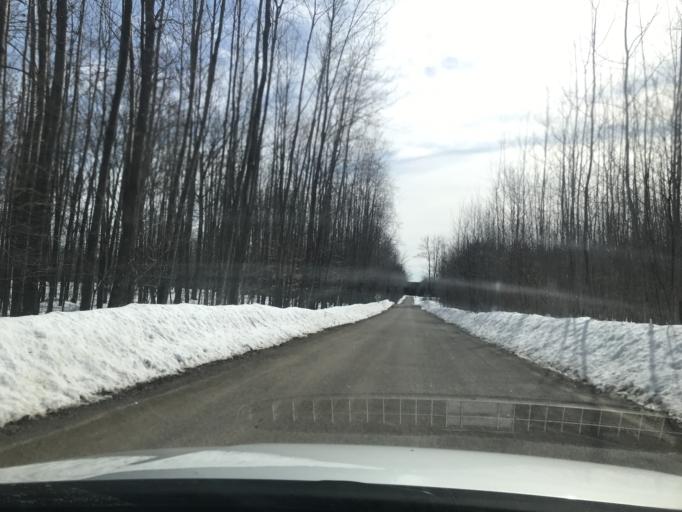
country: US
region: Wisconsin
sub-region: Marinette County
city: Peshtigo
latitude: 45.2983
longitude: -87.8387
